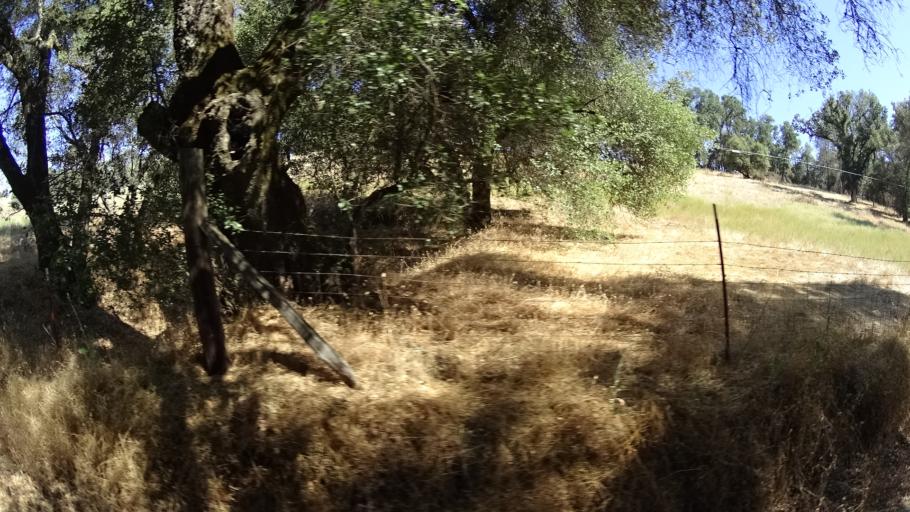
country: US
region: California
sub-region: Calaveras County
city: San Andreas
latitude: 38.1347
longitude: -120.6304
